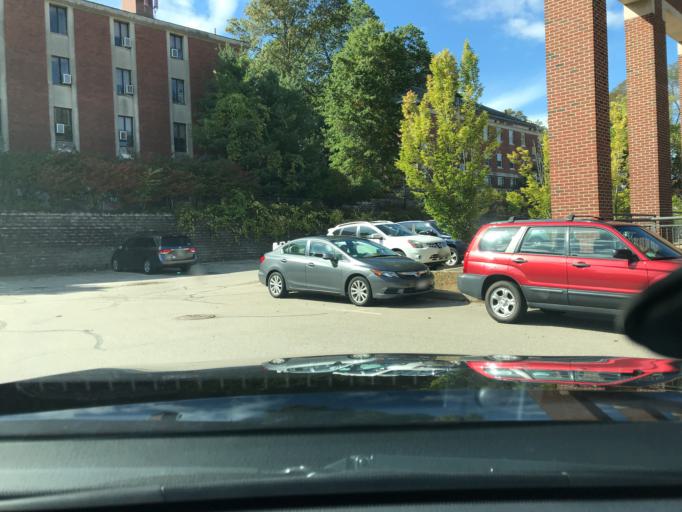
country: US
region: Massachusetts
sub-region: Middlesex County
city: Newton
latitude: 42.3247
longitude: -71.1880
